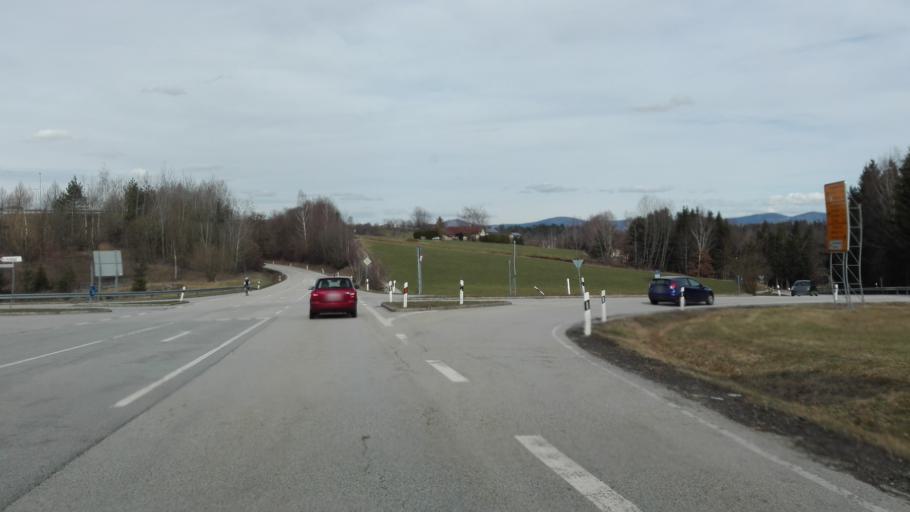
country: DE
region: Bavaria
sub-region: Lower Bavaria
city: Thyrnau
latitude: 48.6026
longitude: 13.5390
